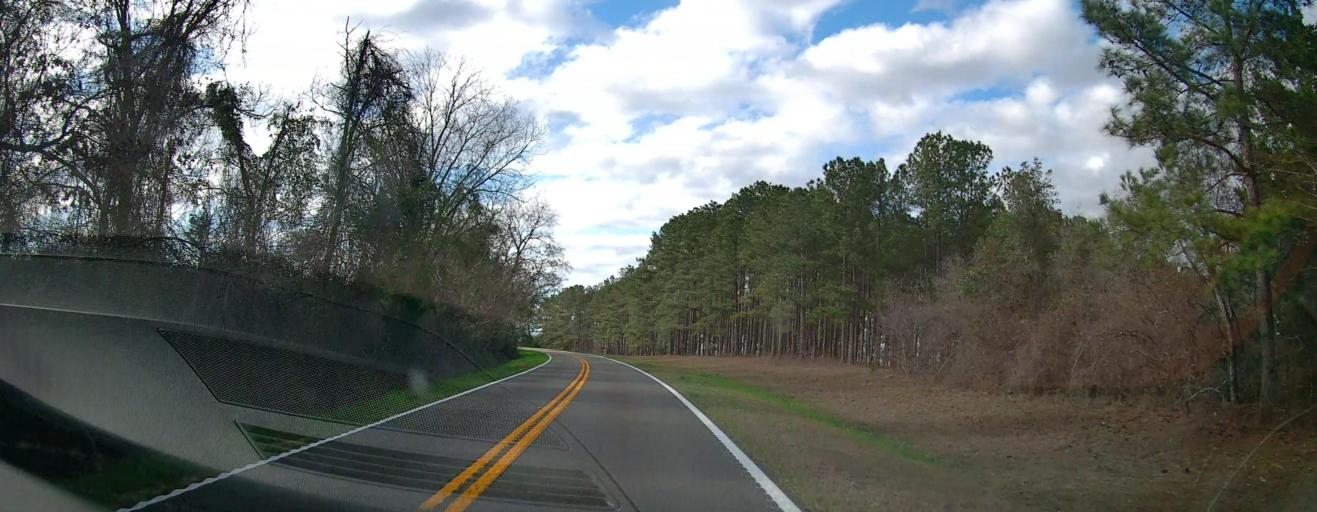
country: US
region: Georgia
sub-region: Marion County
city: Buena Vista
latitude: 32.4432
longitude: -84.5154
